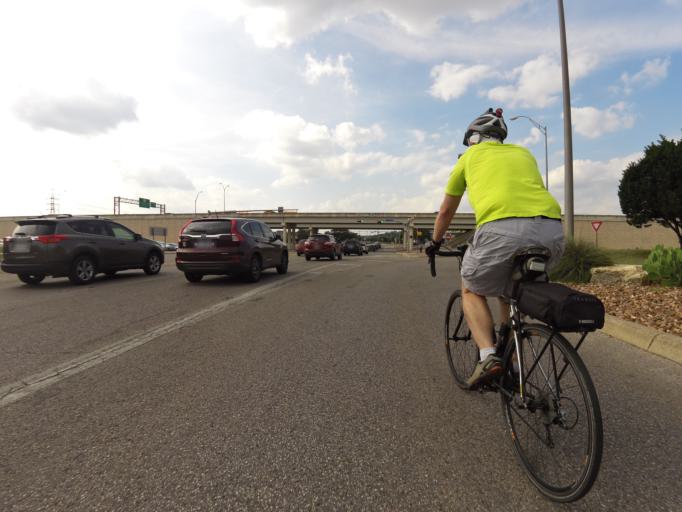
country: US
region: Texas
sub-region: Bexar County
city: Helotes
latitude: 29.5870
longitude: -98.6235
